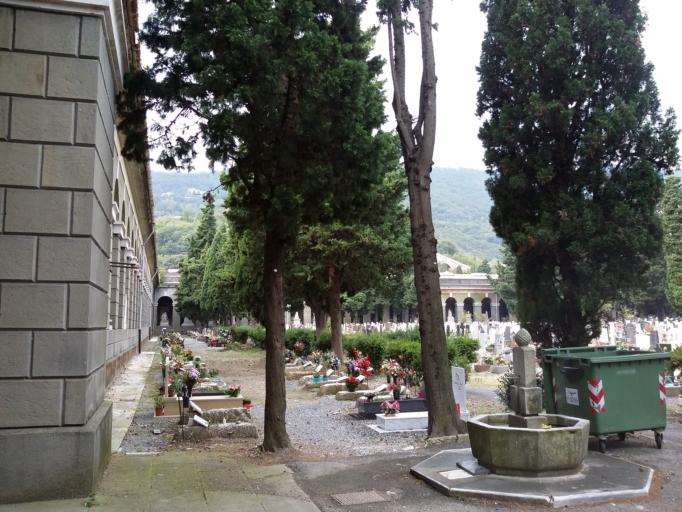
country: IT
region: Liguria
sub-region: Provincia di Genova
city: Genoa
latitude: 44.4288
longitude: 8.9510
